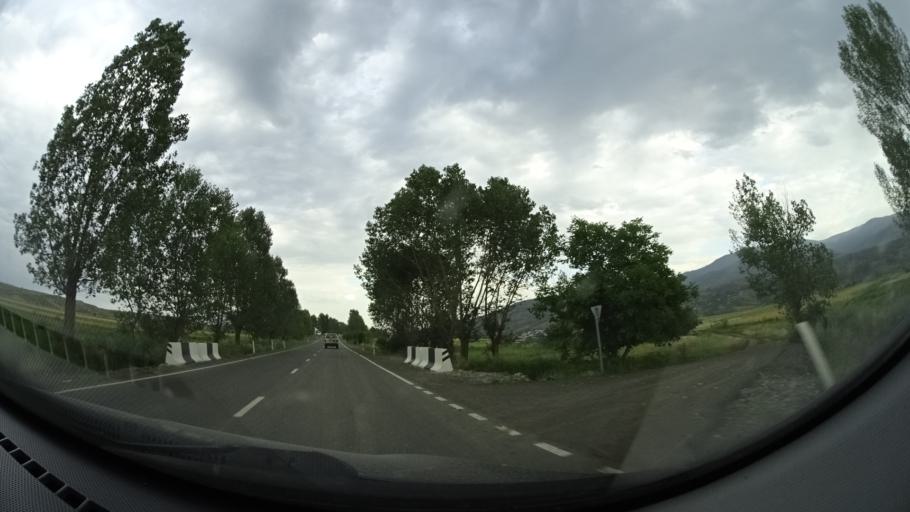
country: GE
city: Vale
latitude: 41.6500
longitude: 42.9161
